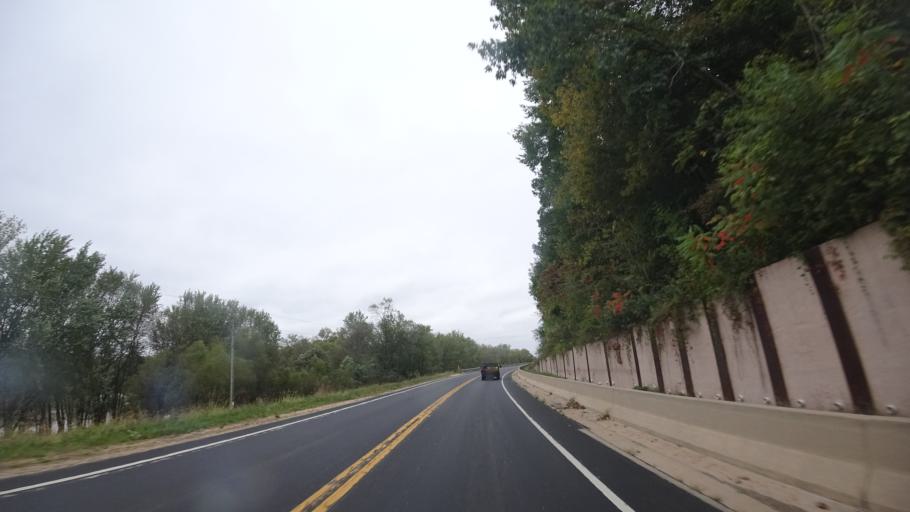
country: US
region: Wisconsin
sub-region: Grant County
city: Boscobel
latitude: 43.1354
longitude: -90.7449
